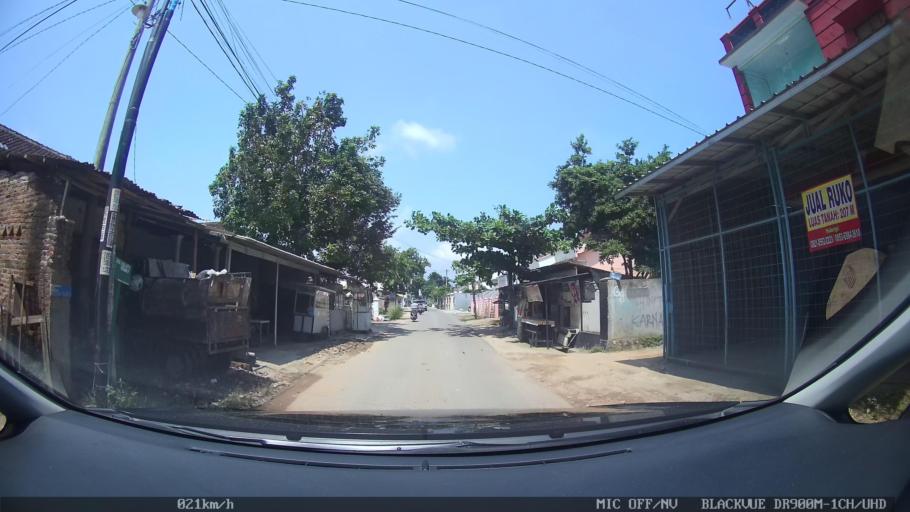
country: ID
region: Lampung
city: Kedaton
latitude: -5.3582
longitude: 105.2765
